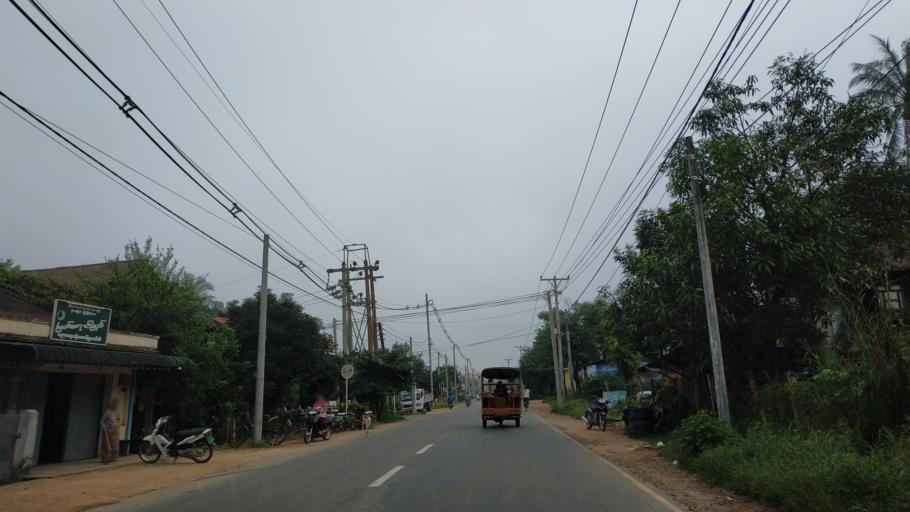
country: MM
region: Tanintharyi
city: Dawei
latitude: 14.0992
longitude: 98.1957
